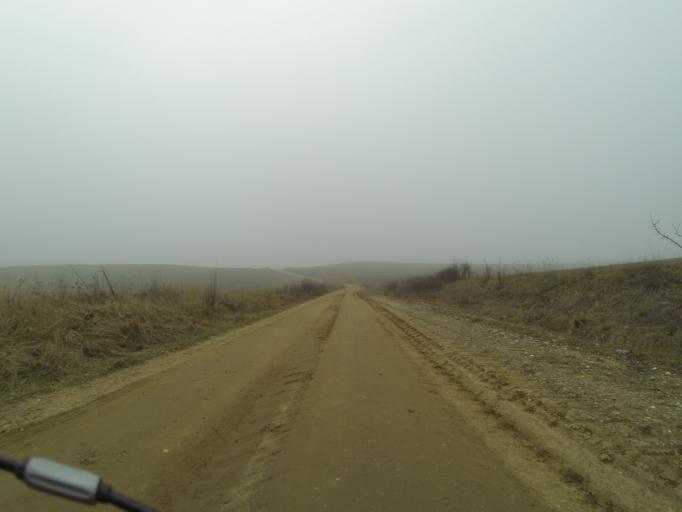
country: RO
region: Mehedinti
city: Dumbrava de Sus
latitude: 44.4809
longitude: 23.0511
